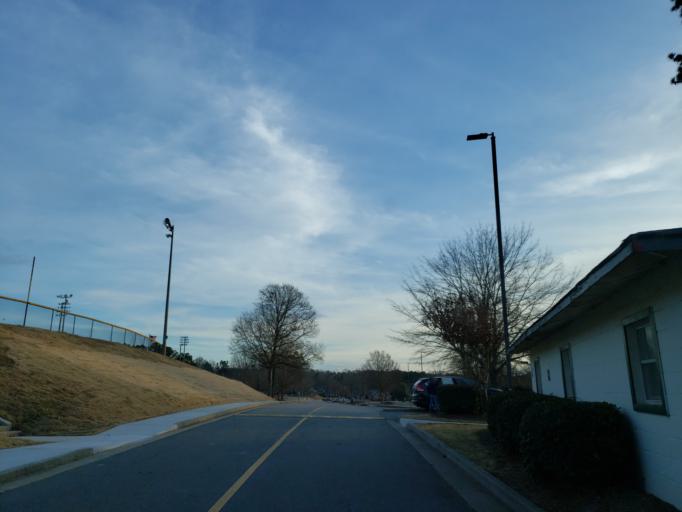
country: US
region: Georgia
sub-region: Cobb County
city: Kennesaw
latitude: 34.0236
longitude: -84.6207
